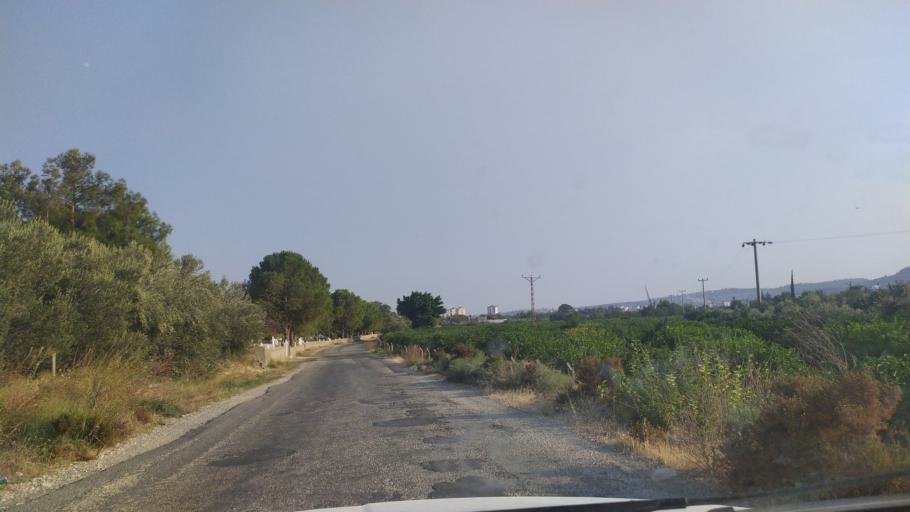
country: TR
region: Mersin
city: Silifke
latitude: 36.4016
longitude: 33.9259
